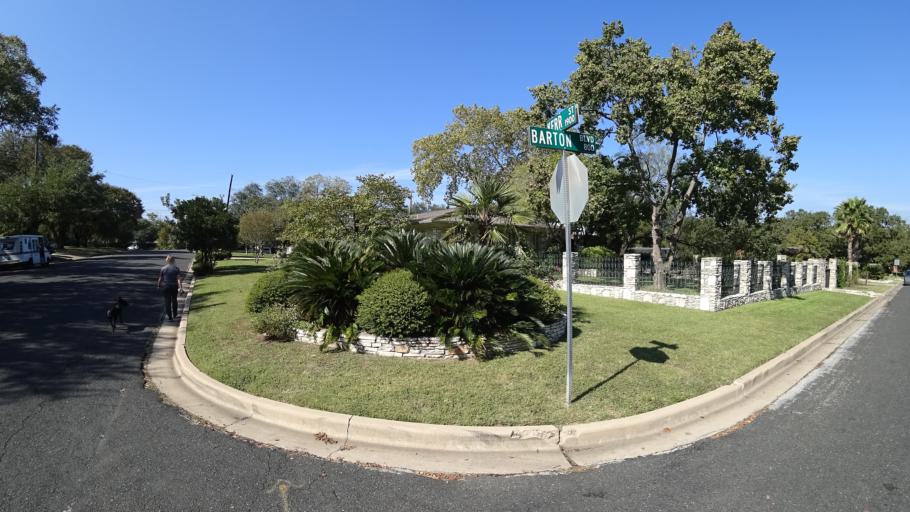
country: US
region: Texas
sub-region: Travis County
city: Austin
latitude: 30.2603
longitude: -97.7677
